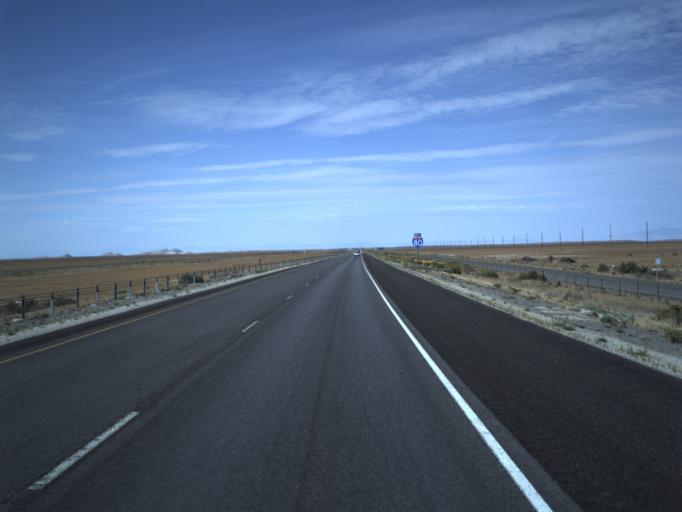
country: US
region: Utah
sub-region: Tooele County
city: Grantsville
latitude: 40.7260
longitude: -113.1443
